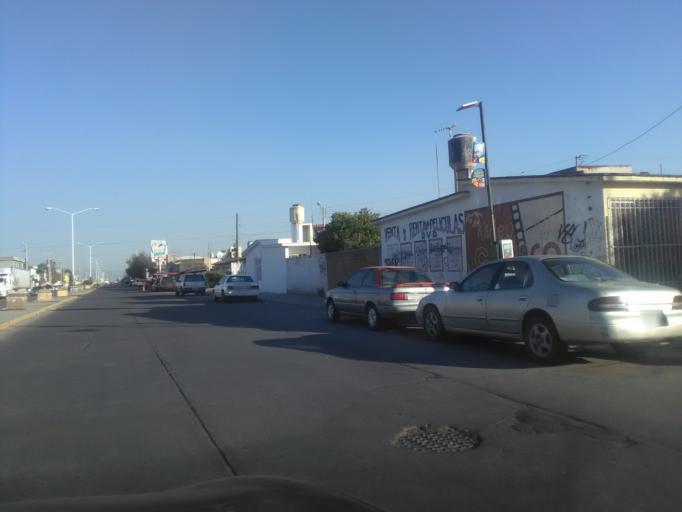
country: MX
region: Durango
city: Victoria de Durango
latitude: 24.0602
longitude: -104.5936
